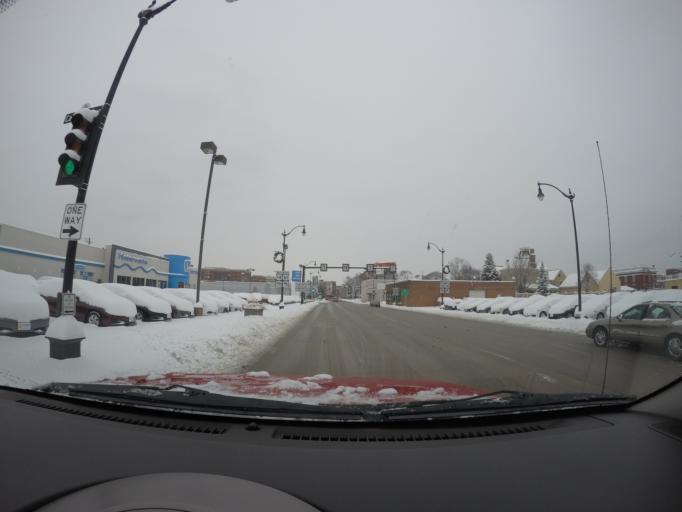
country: US
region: Wisconsin
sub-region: La Crosse County
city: La Crosse
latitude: 43.8078
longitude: -91.2519
